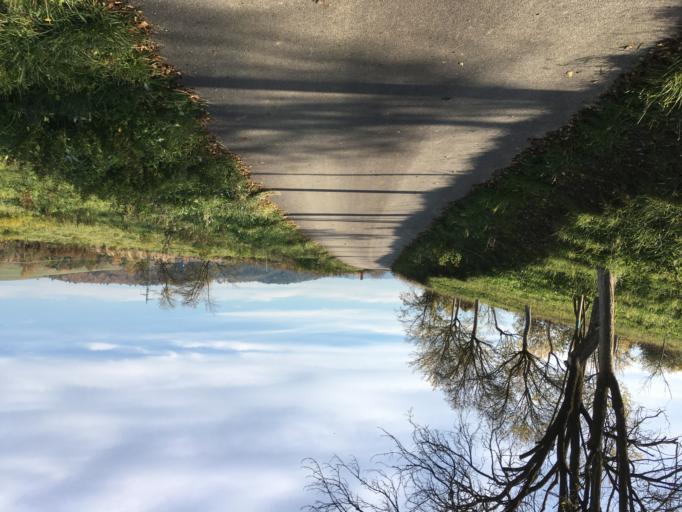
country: SK
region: Trenciansky
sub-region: Okres Povazska Bystrica
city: Povazska Bystrica
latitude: 49.0440
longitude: 18.4249
